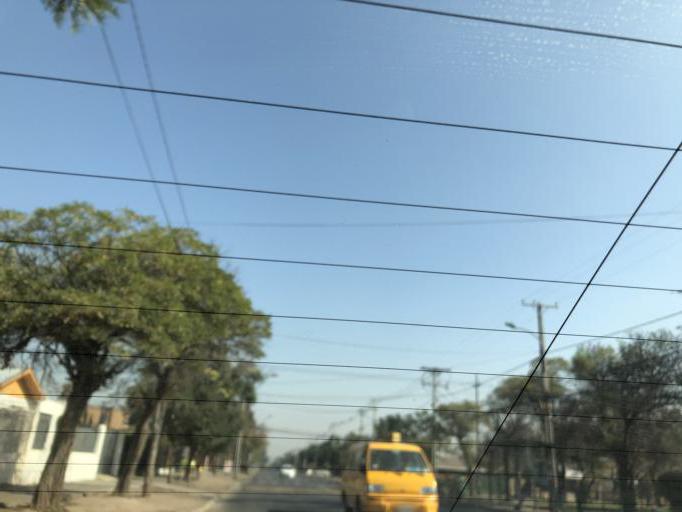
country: CL
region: Santiago Metropolitan
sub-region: Provincia de Cordillera
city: Puente Alto
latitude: -33.6048
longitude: -70.5676
